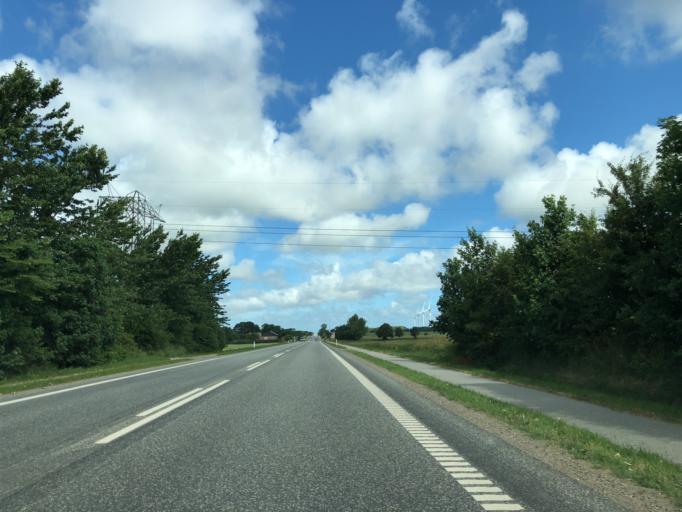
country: DK
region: Central Jutland
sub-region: Holstebro Kommune
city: Holstebro
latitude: 56.4004
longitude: 8.6074
